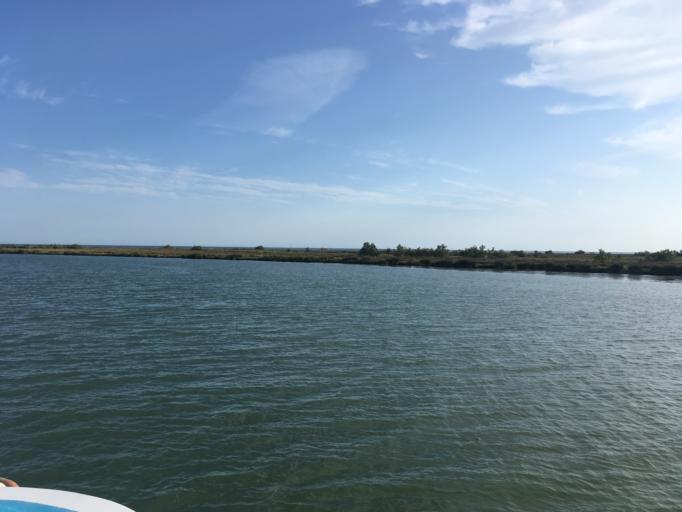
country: FR
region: Provence-Alpes-Cote d'Azur
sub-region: Departement des Bouches-du-Rhone
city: Saintes-Maries-de-la-Mer
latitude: 43.4577
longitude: 4.3899
